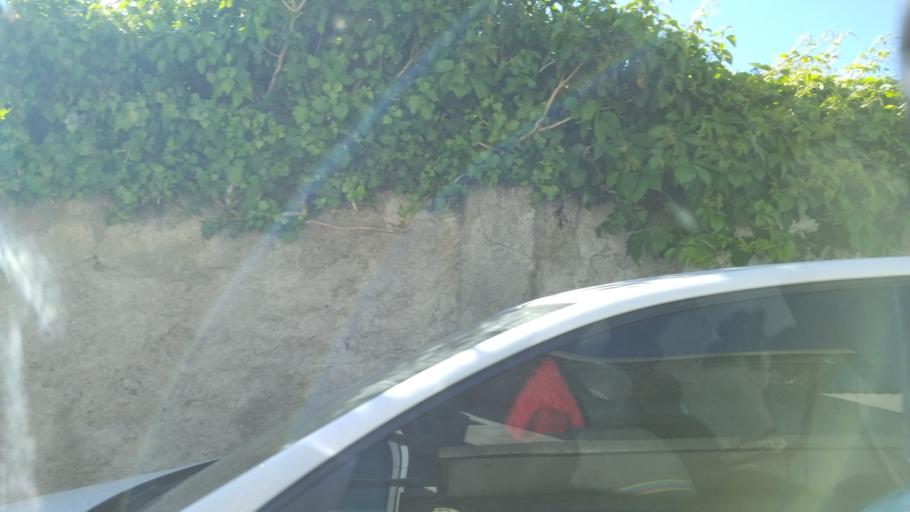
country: AL
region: Shkoder
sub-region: Rrethi i Shkodres
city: Shkoder
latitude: 42.0703
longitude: 19.5218
